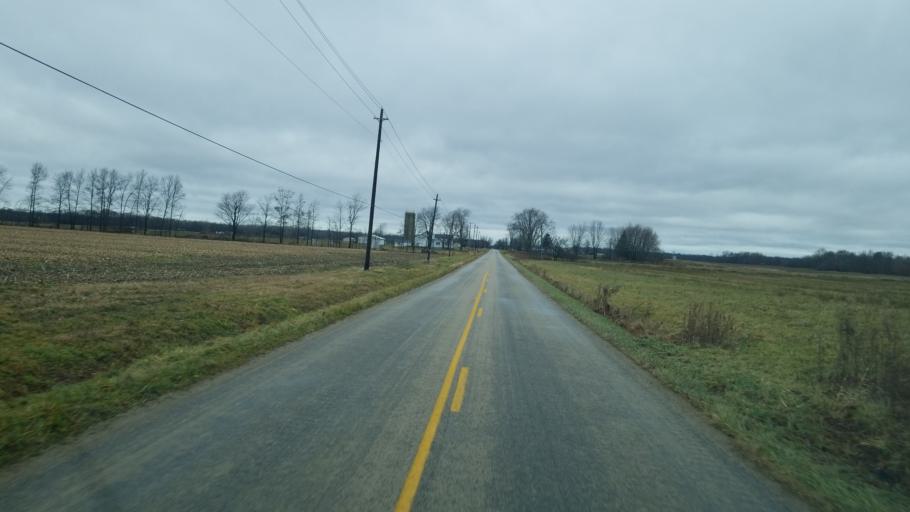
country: US
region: Ohio
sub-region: Ashtabula County
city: Jefferson
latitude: 41.7576
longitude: -80.6227
